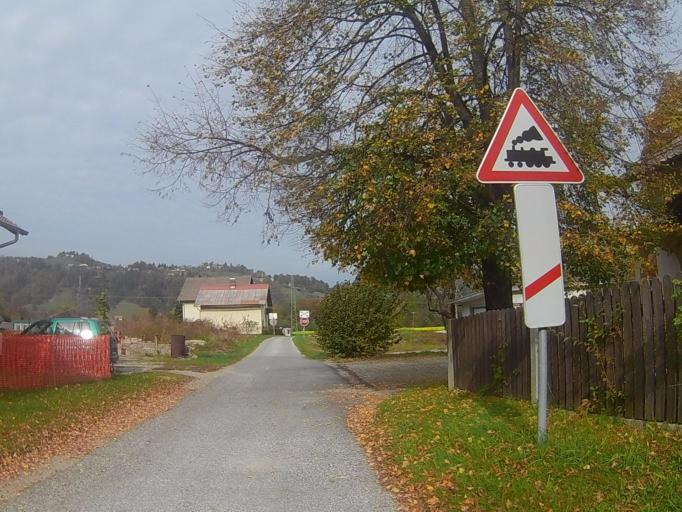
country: SI
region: Maribor
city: Bresternica
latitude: 46.5583
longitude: 15.5684
